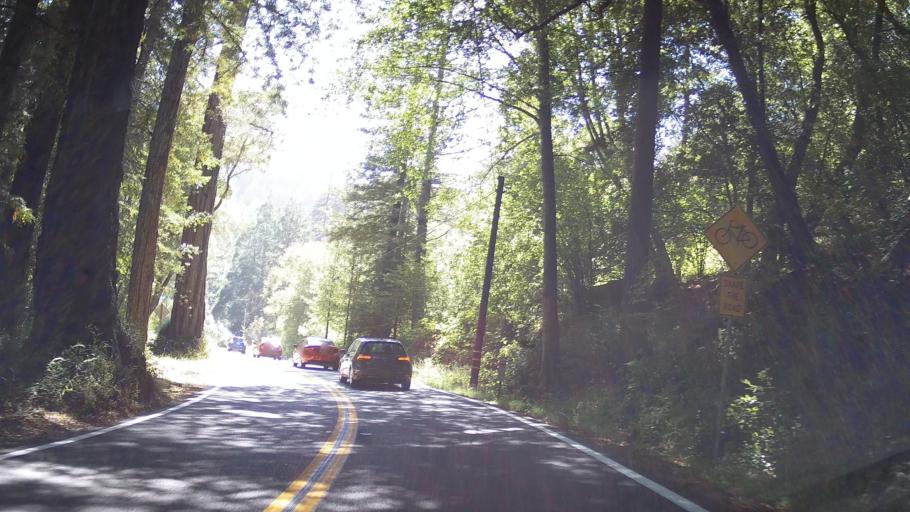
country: US
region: California
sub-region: Marin County
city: Lagunitas-Forest Knolls
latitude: 38.0201
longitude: -122.7285
